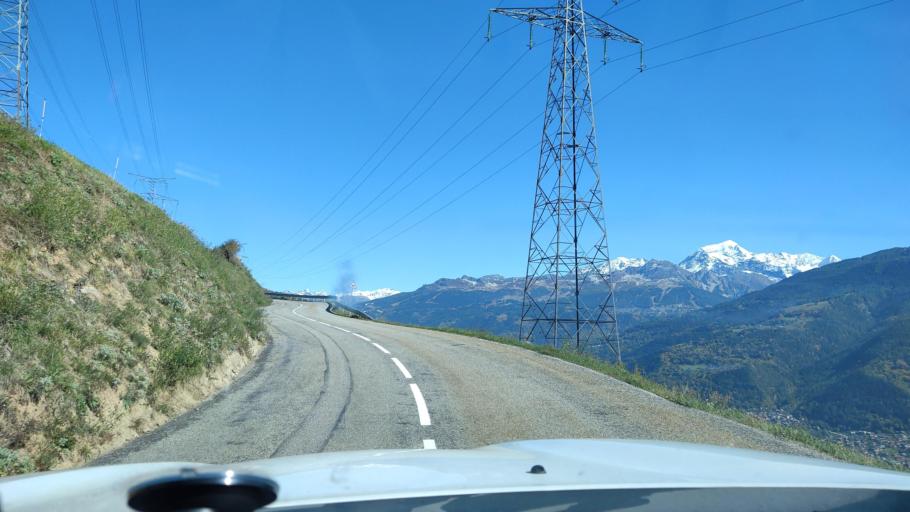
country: FR
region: Rhone-Alpes
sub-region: Departement de la Savoie
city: Aime
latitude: 45.5644
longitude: 6.6418
